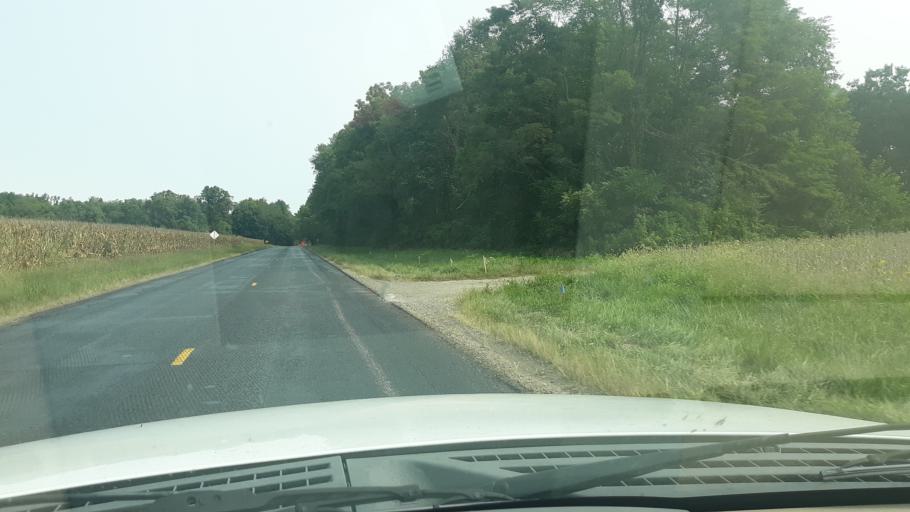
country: US
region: Illinois
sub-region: Edwards County
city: Grayville
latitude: 38.2815
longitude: -87.9828
